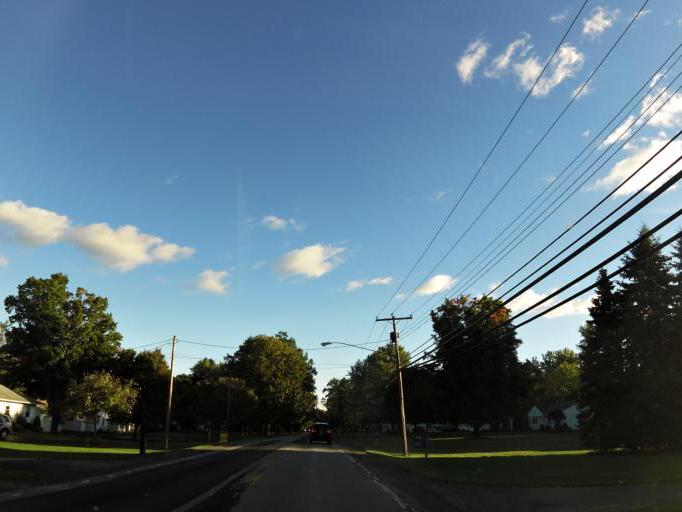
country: US
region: New York
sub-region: Erie County
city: Billington Heights
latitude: 42.7905
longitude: -78.6211
